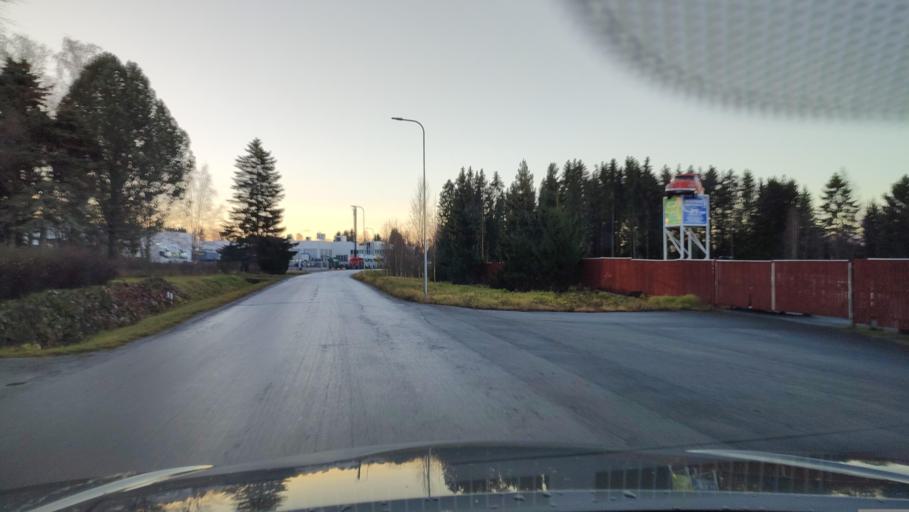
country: FI
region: Ostrobothnia
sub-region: Sydosterbotten
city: Naerpes
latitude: 62.4770
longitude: 21.3686
